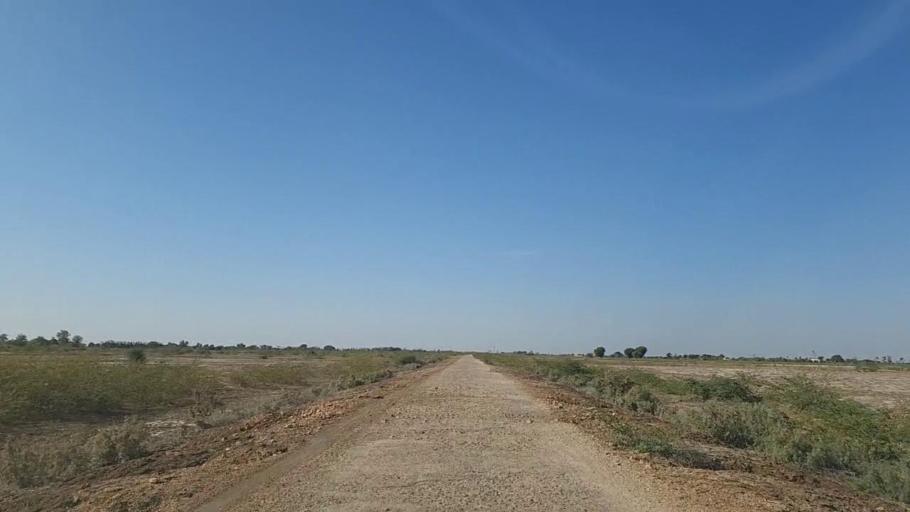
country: PK
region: Sindh
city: Kunri
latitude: 25.2427
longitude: 69.4979
